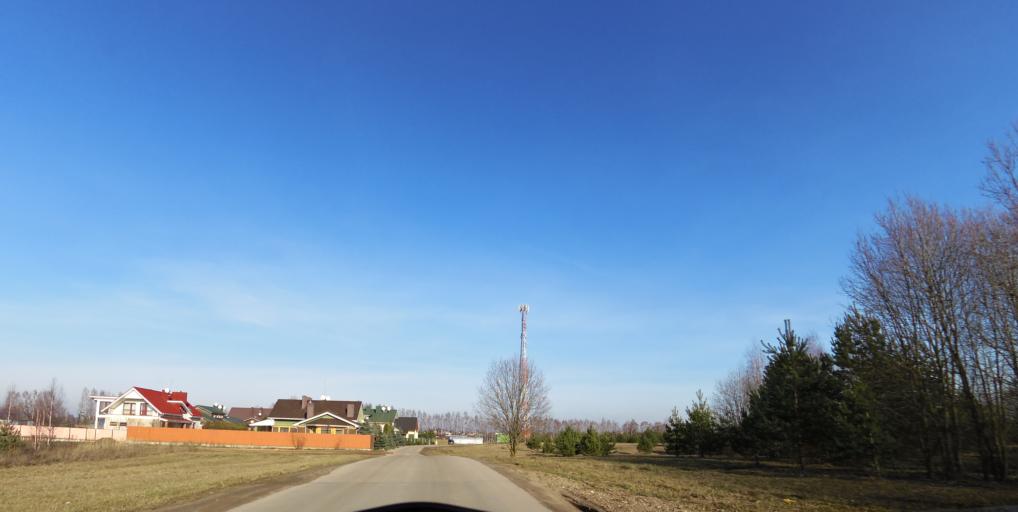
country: LT
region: Vilnius County
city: Pilaite
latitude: 54.7081
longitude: 25.1602
